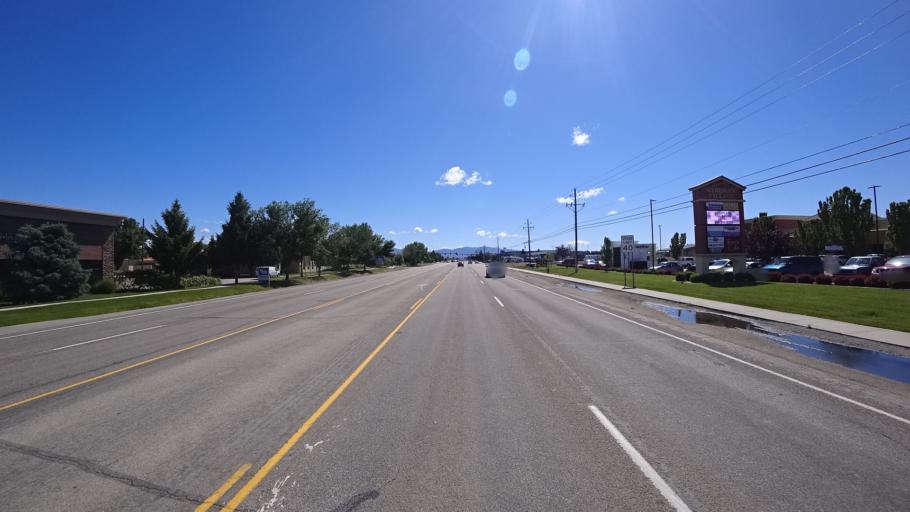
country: US
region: Idaho
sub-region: Ada County
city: Meridian
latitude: 43.6194
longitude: -116.3644
